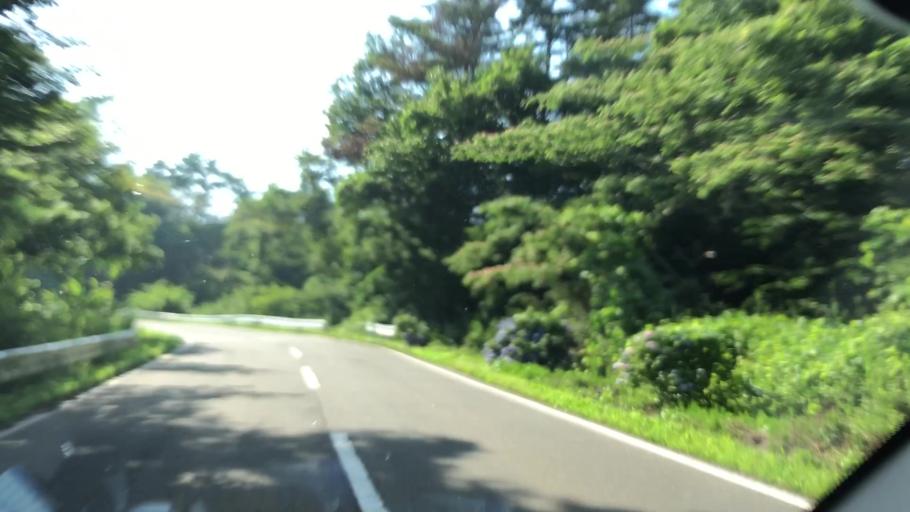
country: JP
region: Miyagi
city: Shiroishi
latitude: 38.0241
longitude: 140.5600
